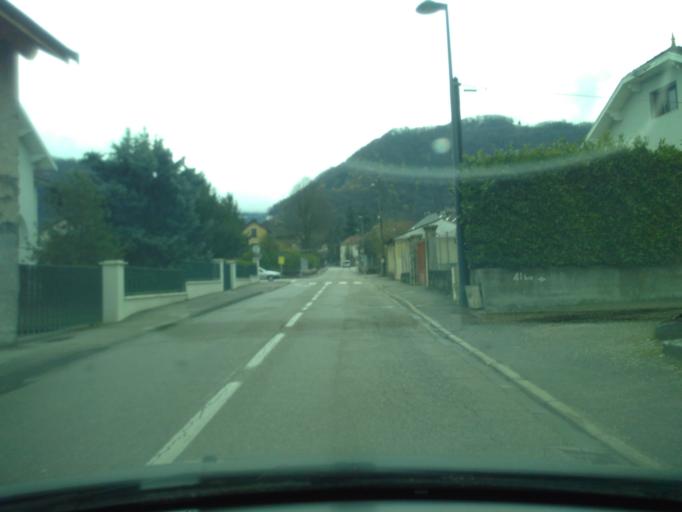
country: FR
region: Rhone-Alpes
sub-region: Departement de l'Isere
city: Domene
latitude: 45.2060
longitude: 5.8349
